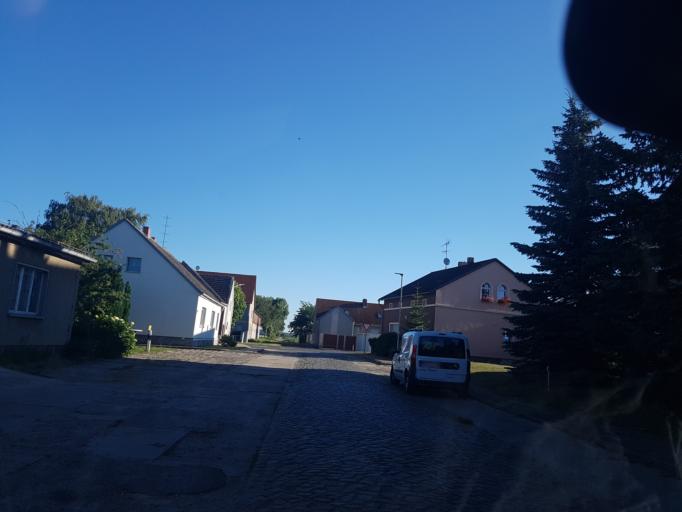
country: DE
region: Brandenburg
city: Juterbog
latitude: 51.9285
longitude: 13.1390
